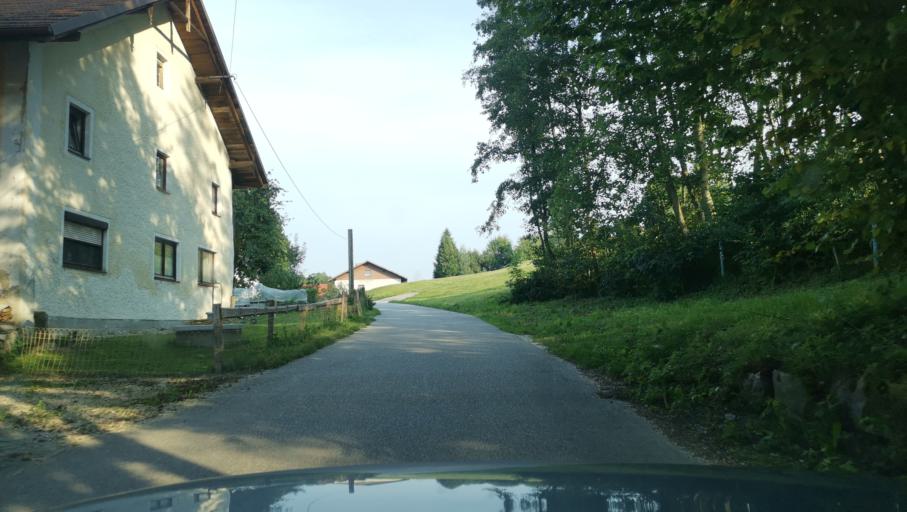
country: DE
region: Bavaria
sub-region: Lower Bavaria
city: Obernzell
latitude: 48.3713
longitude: 13.6573
